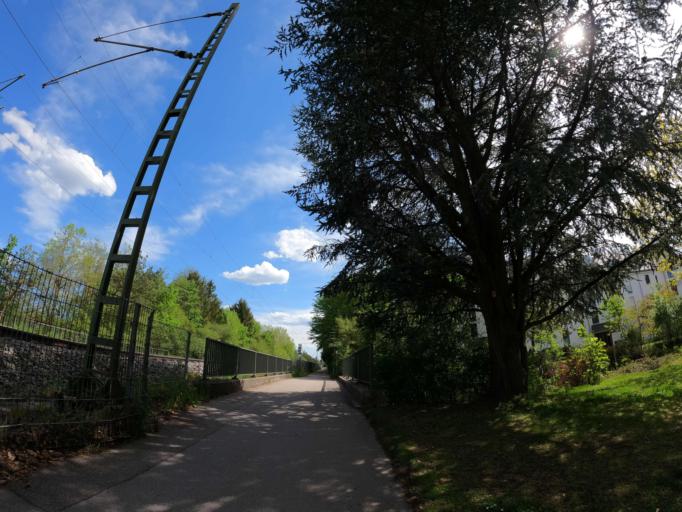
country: DE
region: Bavaria
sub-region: Upper Bavaria
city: Unterhaching
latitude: 48.0744
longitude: 11.6107
